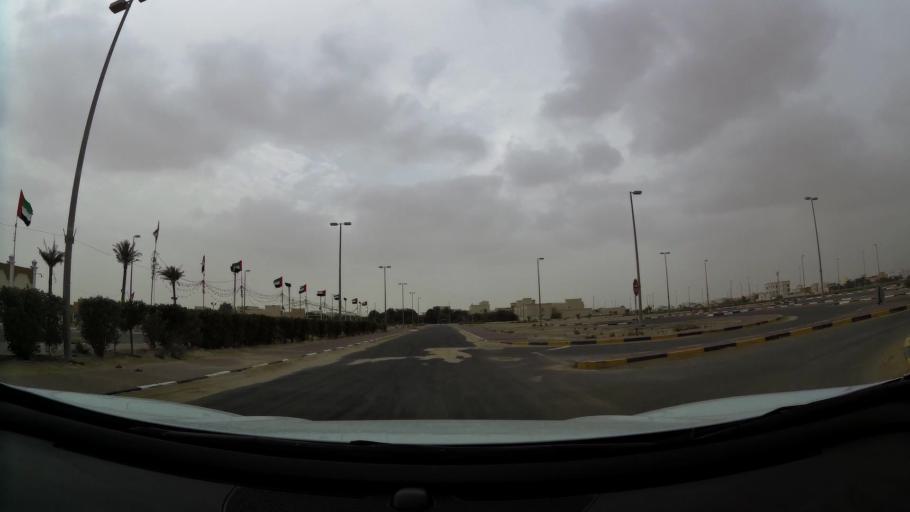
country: AE
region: Abu Dhabi
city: Abu Dhabi
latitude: 24.3726
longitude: 54.6664
